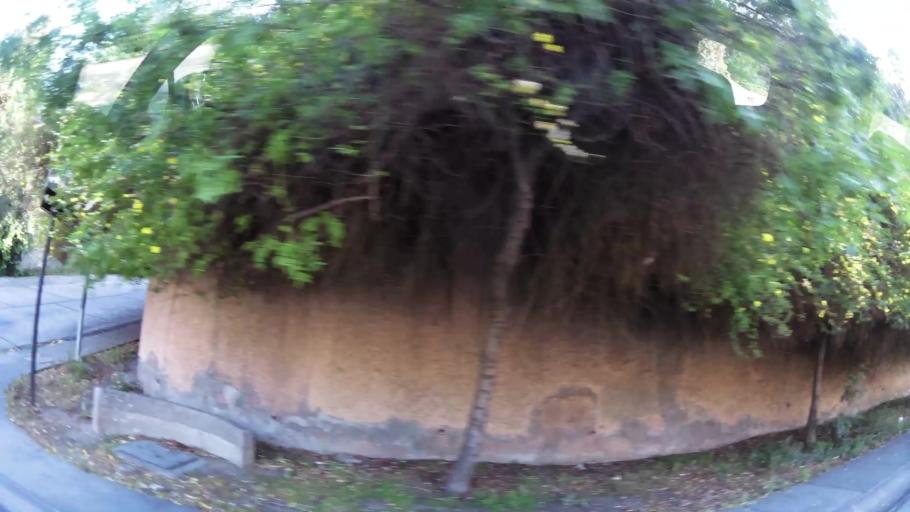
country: CL
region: Santiago Metropolitan
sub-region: Provincia de Santiago
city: Villa Presidente Frei, Nunoa, Santiago, Chile
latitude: -33.3716
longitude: -70.4977
